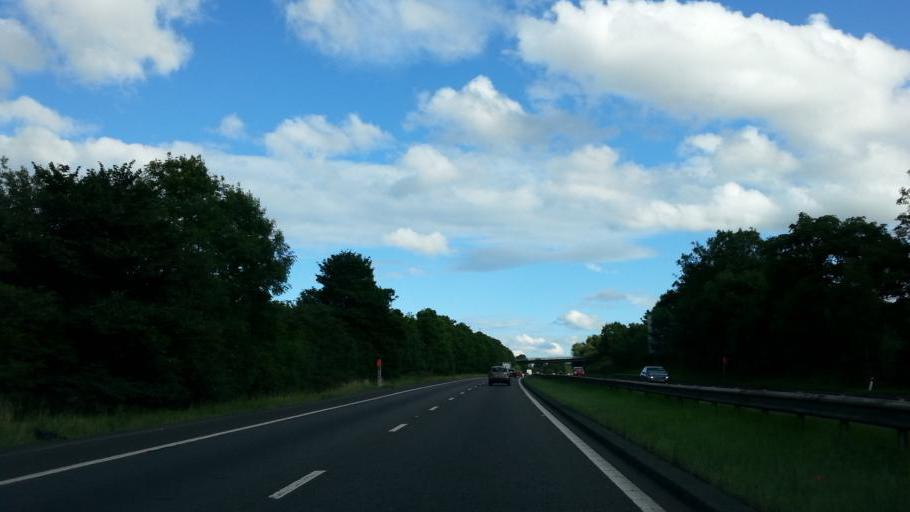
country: GB
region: England
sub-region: Doncaster
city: Stainton
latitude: 53.4695
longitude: -1.1370
